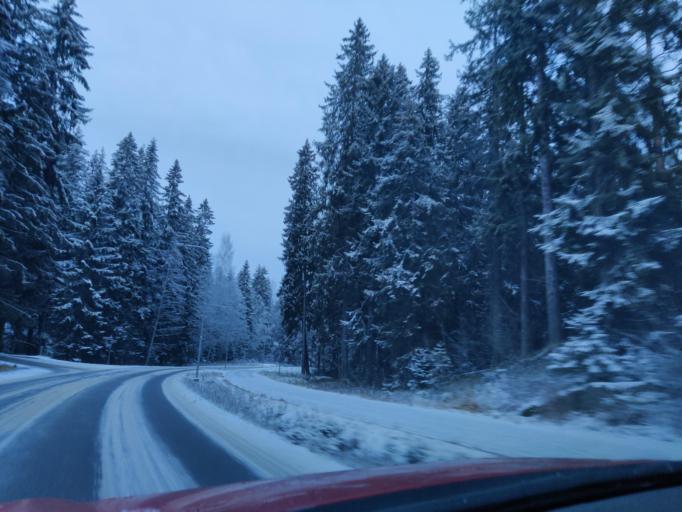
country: FI
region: Pirkanmaa
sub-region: Tampere
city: Tampere
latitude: 61.5101
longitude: 23.7942
